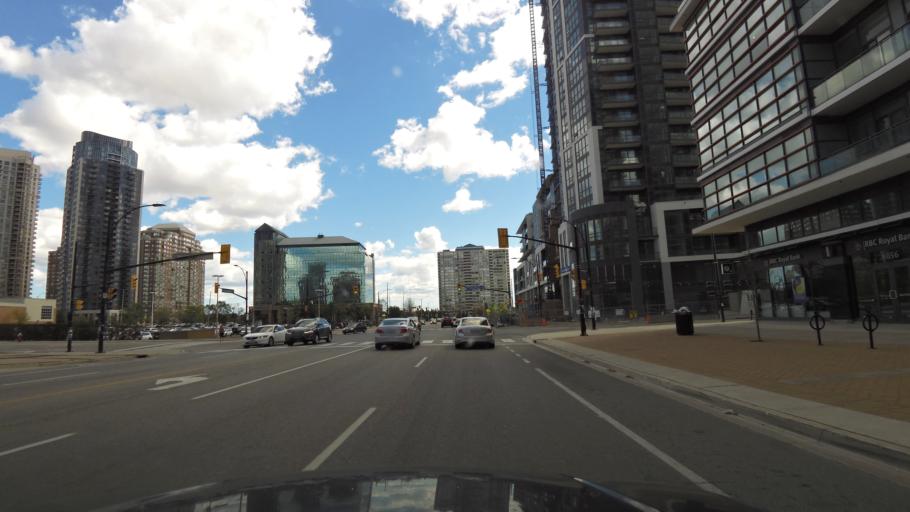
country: CA
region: Ontario
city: Mississauga
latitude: 43.5863
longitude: -79.6467
